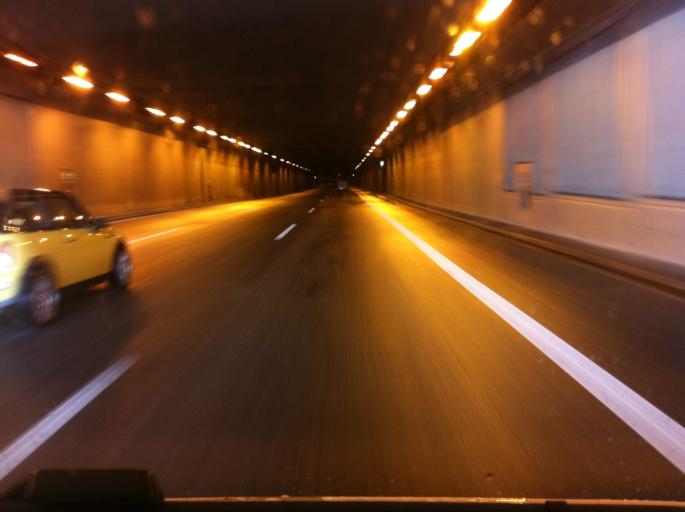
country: DE
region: North Rhine-Westphalia
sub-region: Regierungsbezirk Dusseldorf
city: Meerbusch
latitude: 51.2842
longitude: 6.6876
